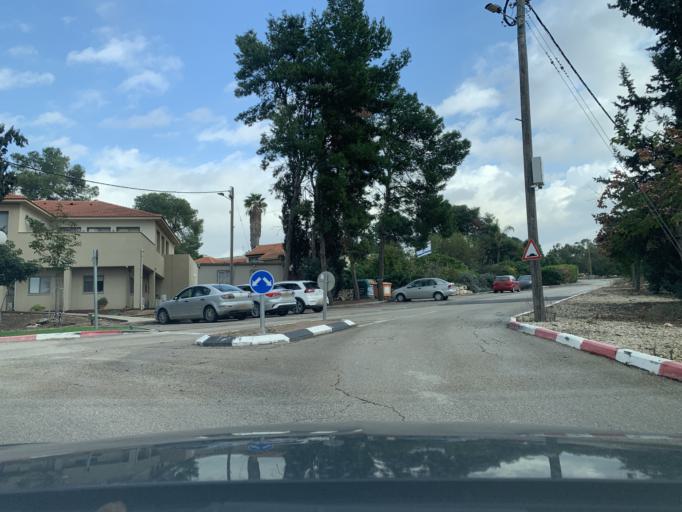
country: IL
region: Central District
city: Rosh Ha'Ayin
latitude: 32.0598
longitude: 34.9487
